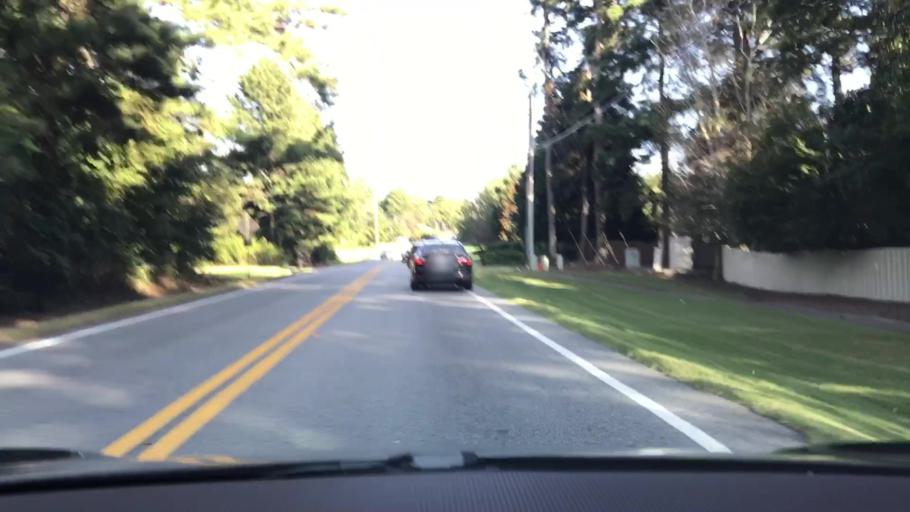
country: US
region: Georgia
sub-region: Gwinnett County
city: Dacula
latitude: 34.0401
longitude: -83.9175
